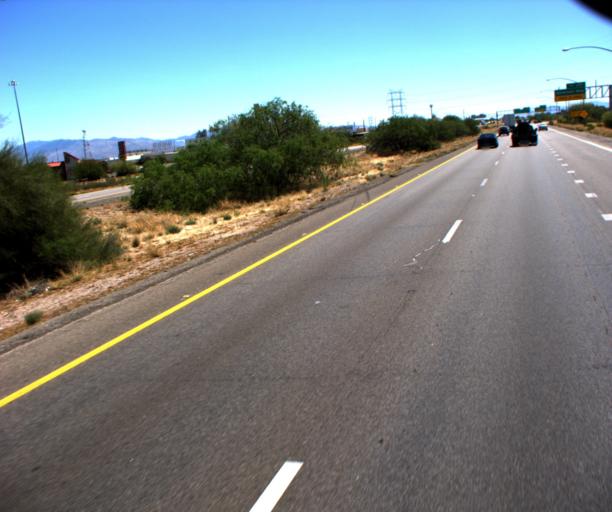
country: US
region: Arizona
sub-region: Pima County
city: Tucson
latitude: 32.1614
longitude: -110.9165
